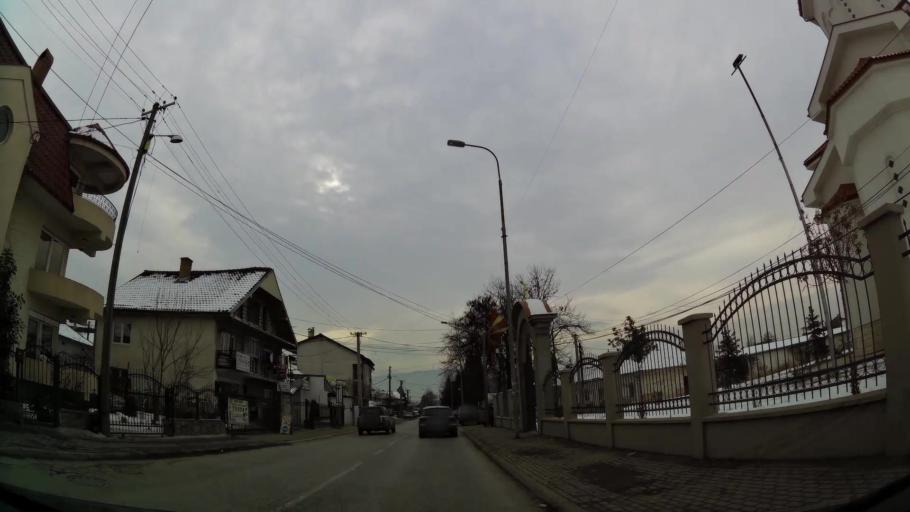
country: MK
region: Butel
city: Butel
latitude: 42.0384
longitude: 21.4474
